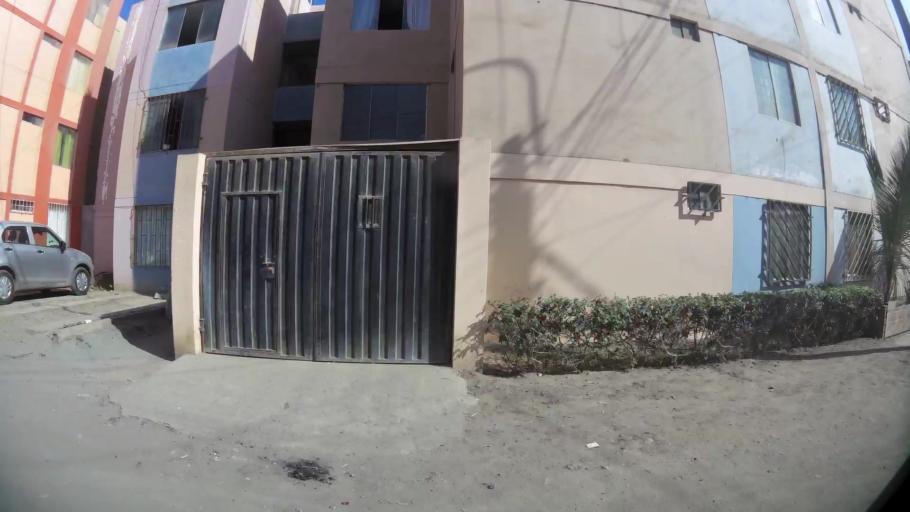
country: PE
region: Lima
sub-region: Huaura
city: Huacho
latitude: -11.1258
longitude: -77.6113
